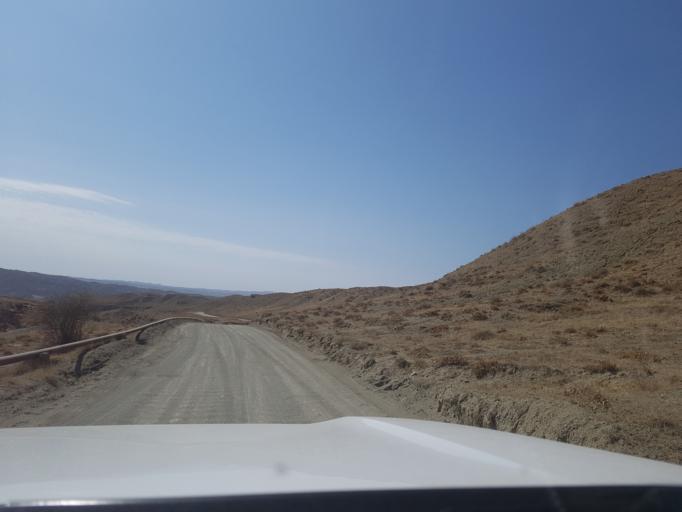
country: TM
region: Ahal
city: Baharly
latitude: 38.2458
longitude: 56.8916
